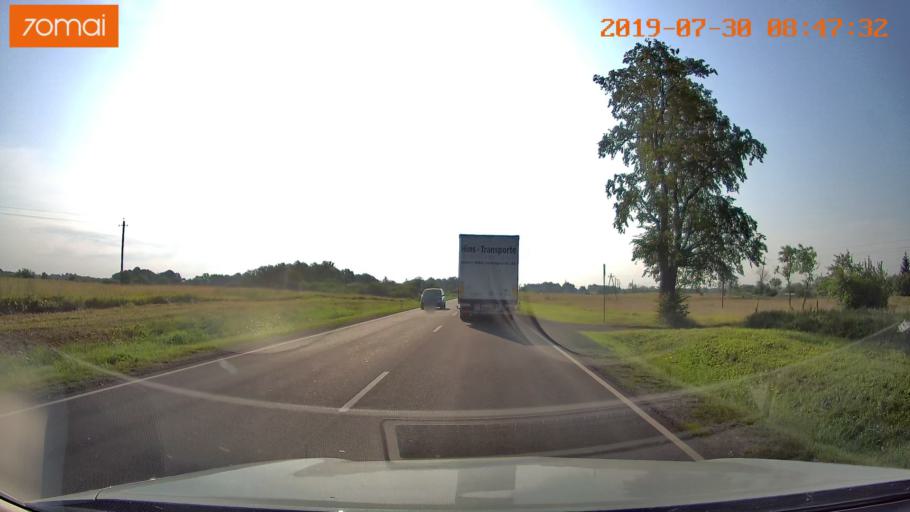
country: RU
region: Kaliningrad
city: Chernyakhovsk
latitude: 54.6213
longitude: 21.8944
